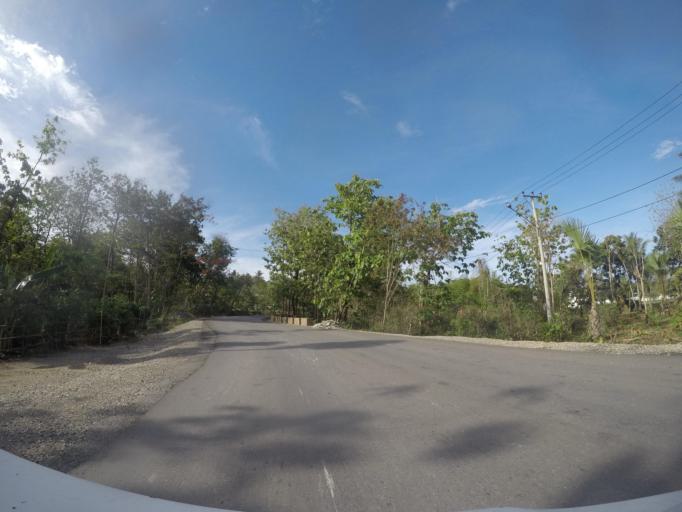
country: TL
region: Baucau
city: Baucau
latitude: -8.4946
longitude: 126.4549
